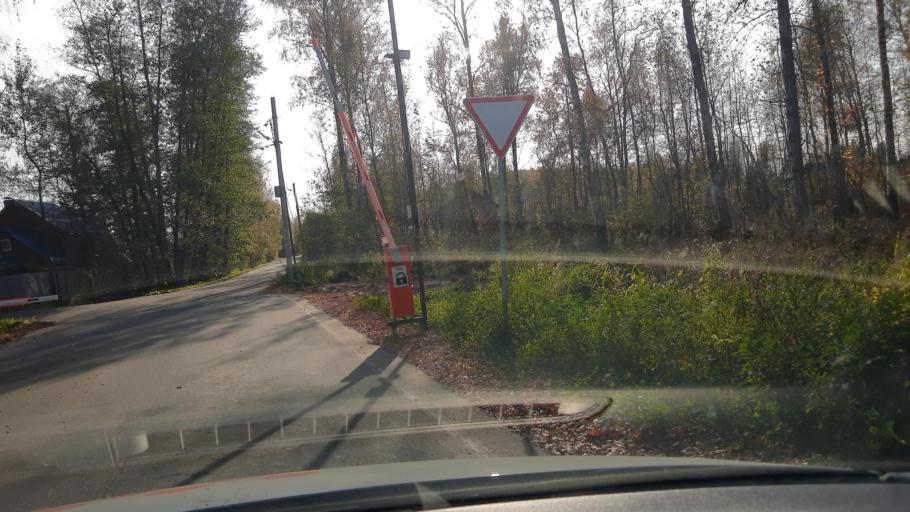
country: RU
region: Moskovskaya
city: Imeni Vorovskogo
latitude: 55.7839
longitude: 38.3607
